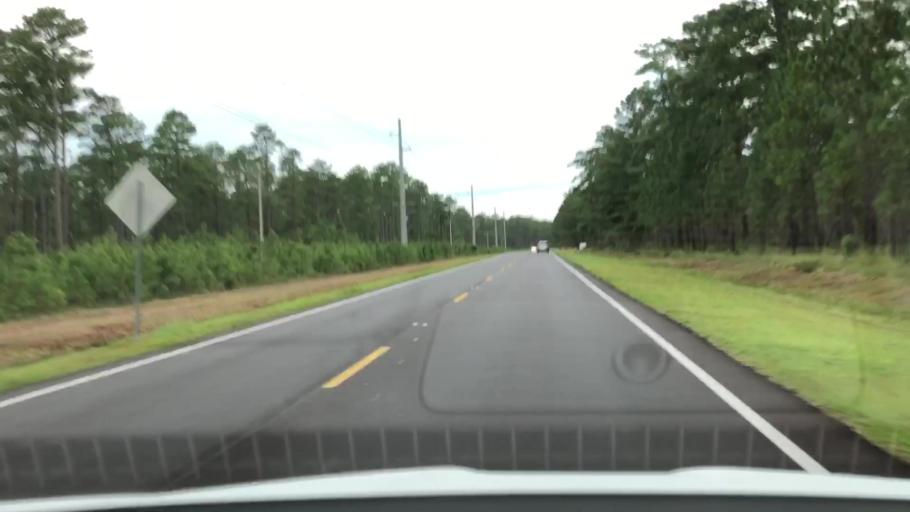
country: US
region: North Carolina
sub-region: Jones County
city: Maysville
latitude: 34.8139
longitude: -77.1411
